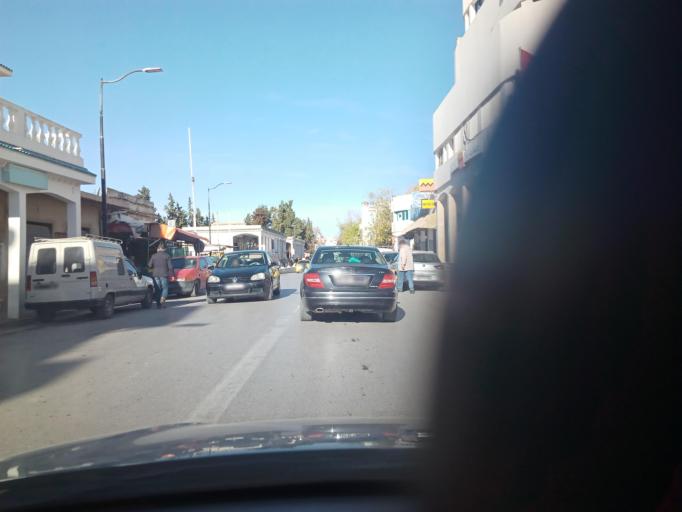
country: TN
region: Kef
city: El Kef
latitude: 36.1782
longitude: 8.7139
